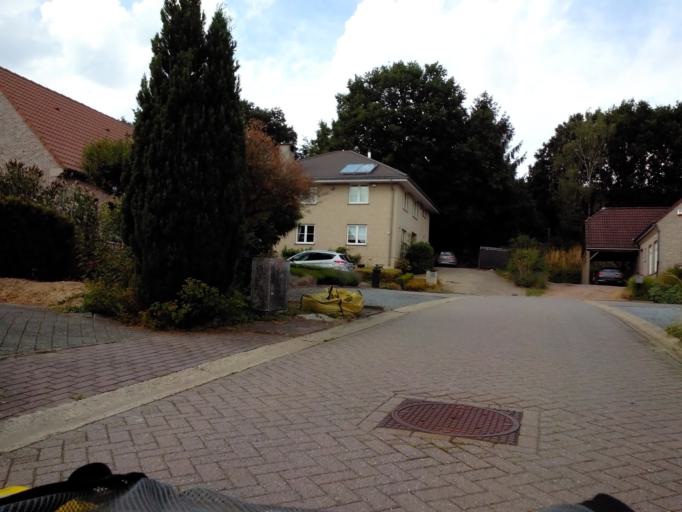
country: BE
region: Flanders
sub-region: Provincie Vlaams-Brabant
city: Holsbeek
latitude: 50.8945
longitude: 4.7812
